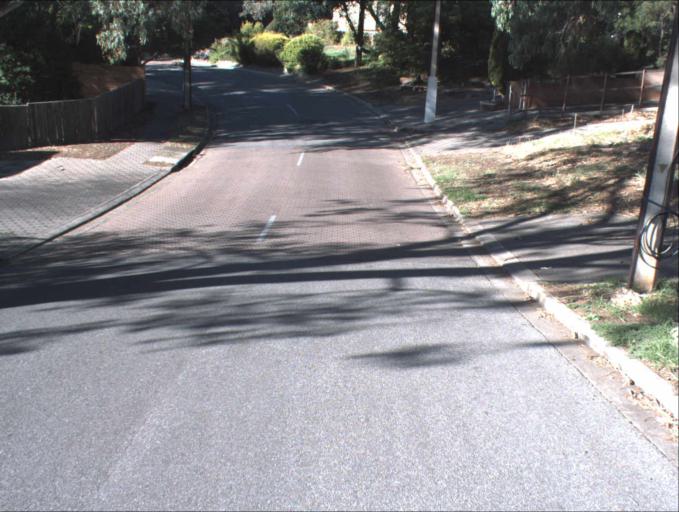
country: AU
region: South Australia
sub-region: Campbelltown
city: Paradise
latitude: -34.8689
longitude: 138.6539
